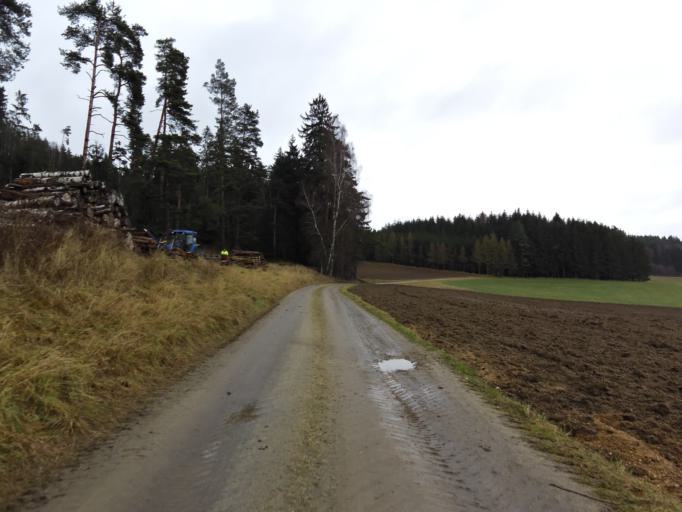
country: DE
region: Bavaria
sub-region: Upper Franconia
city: Wunsiedel
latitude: 50.0662
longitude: 12.0327
